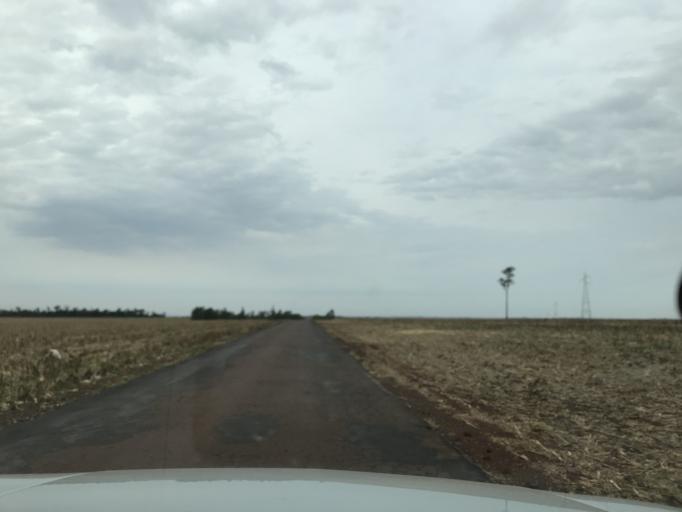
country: BR
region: Parana
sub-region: Palotina
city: Palotina
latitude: -24.2848
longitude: -53.7882
